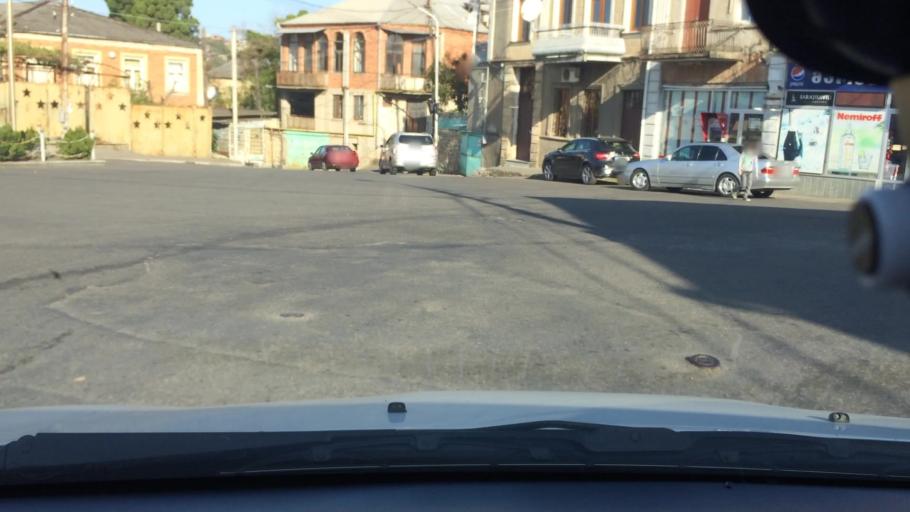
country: GE
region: Imereti
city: Kutaisi
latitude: 42.2722
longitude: 42.7119
